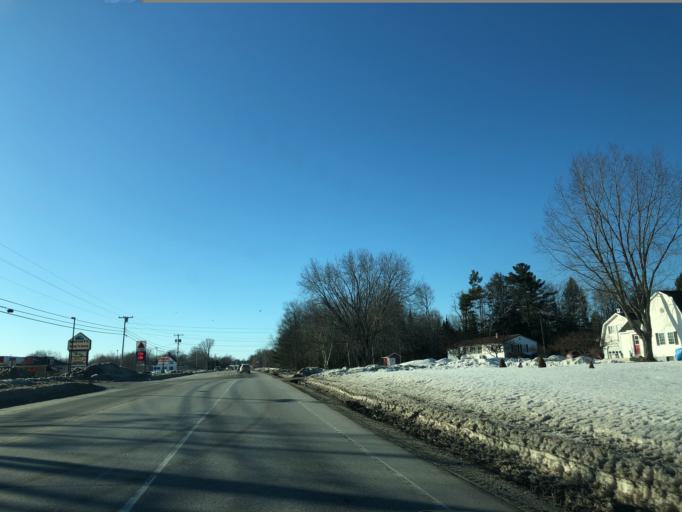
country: US
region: Maine
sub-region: Penobscot County
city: Kenduskeag
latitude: 44.9829
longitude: -69.0013
